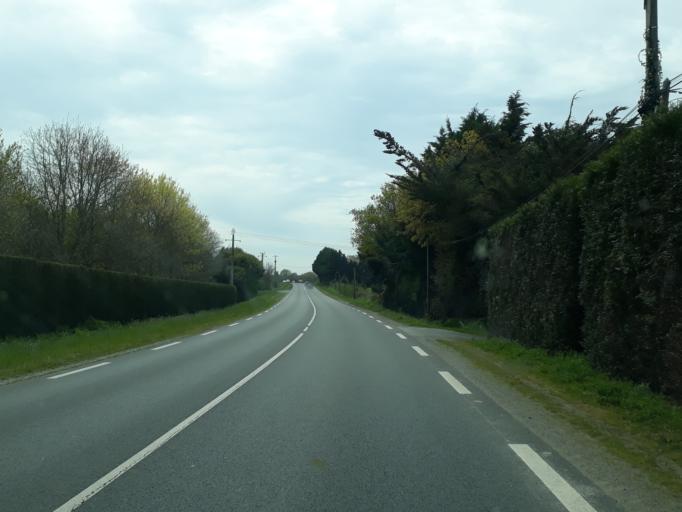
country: FR
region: Pays de la Loire
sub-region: Departement de la Loire-Atlantique
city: Guerande
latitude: 47.3490
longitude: -2.4252
